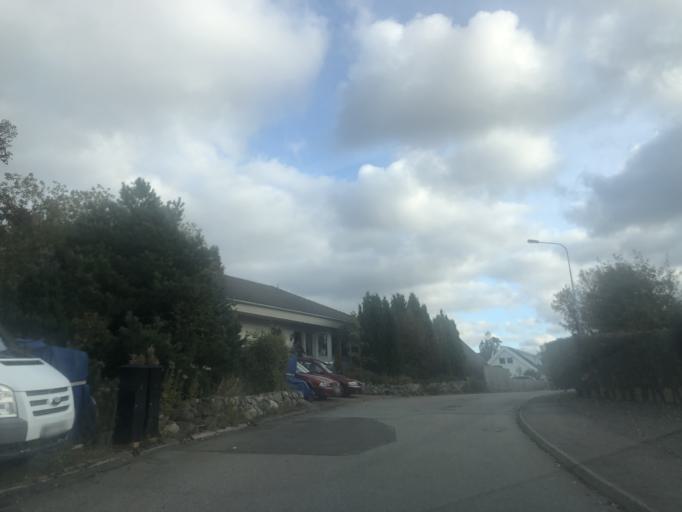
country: SE
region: Vaestra Goetaland
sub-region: Goteborg
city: Majorna
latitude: 57.6365
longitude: 11.9481
